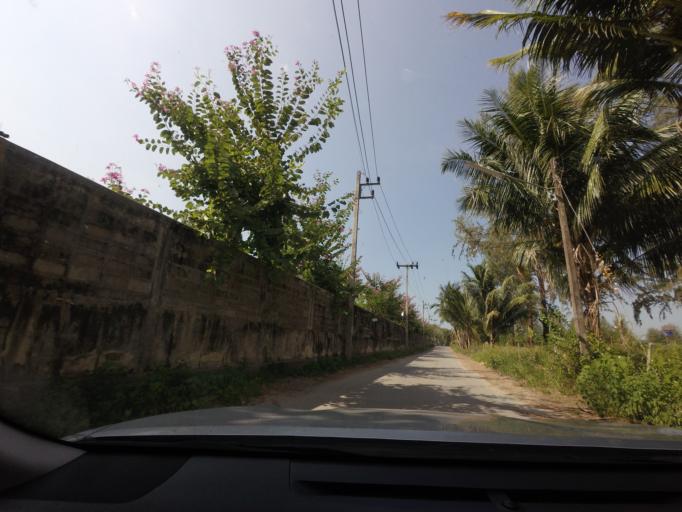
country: TH
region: Phangnga
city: Ban Khao Lak
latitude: 8.6637
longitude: 98.2499
